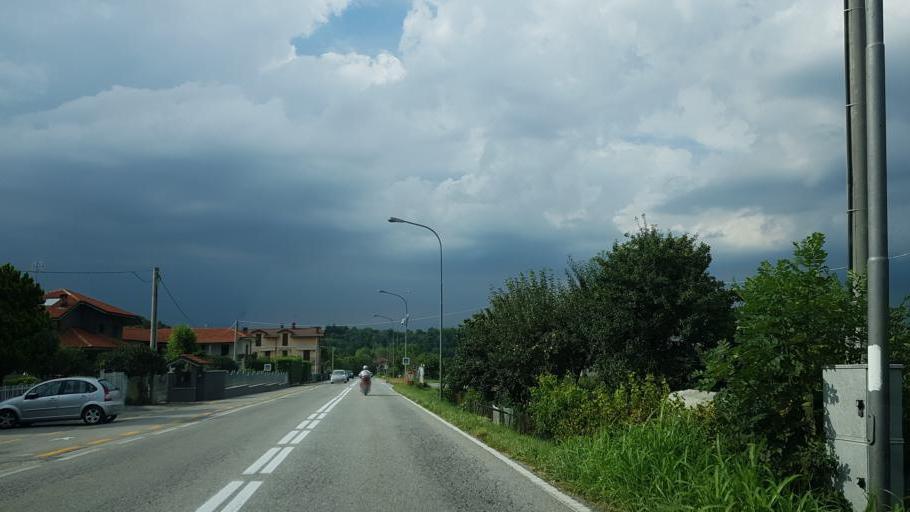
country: IT
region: Piedmont
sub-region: Provincia di Cuneo
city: Vignolo
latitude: 44.3631
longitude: 7.4751
